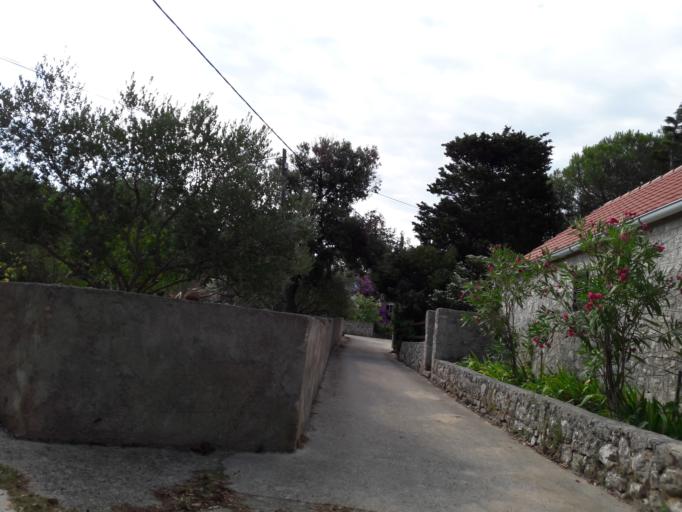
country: HR
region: Licko-Senjska
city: Novalja
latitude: 44.3779
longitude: 14.6922
